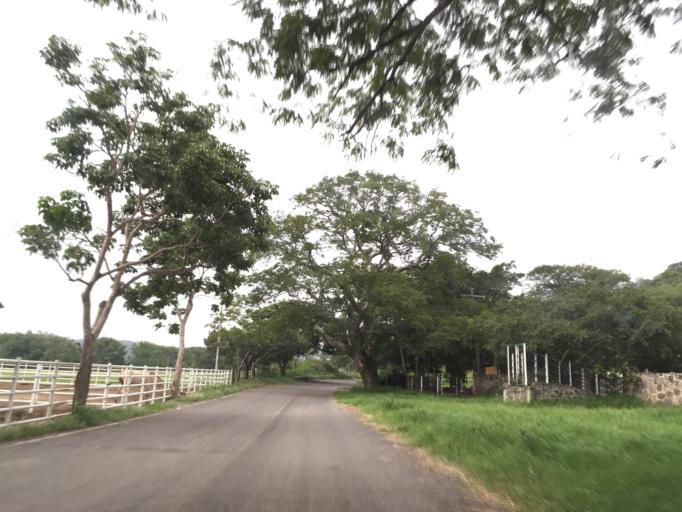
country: MX
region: Colima
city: Comala
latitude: 19.3991
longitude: -103.8029
